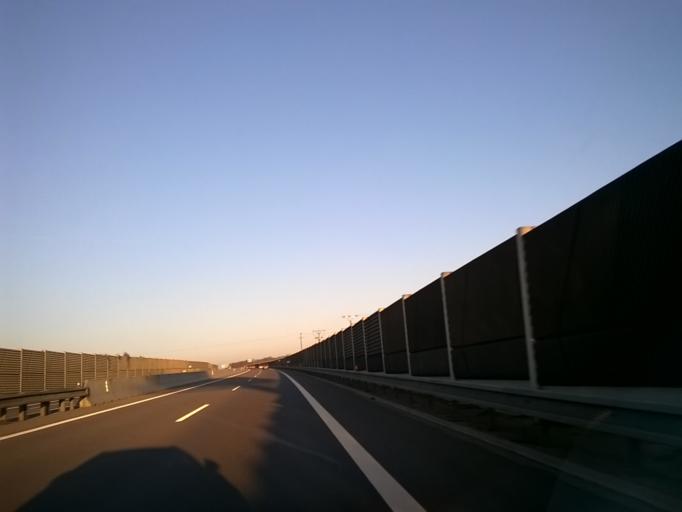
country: SK
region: Nitriansky
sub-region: Okres Nitra
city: Nitra
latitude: 48.2993
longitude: 18.1249
